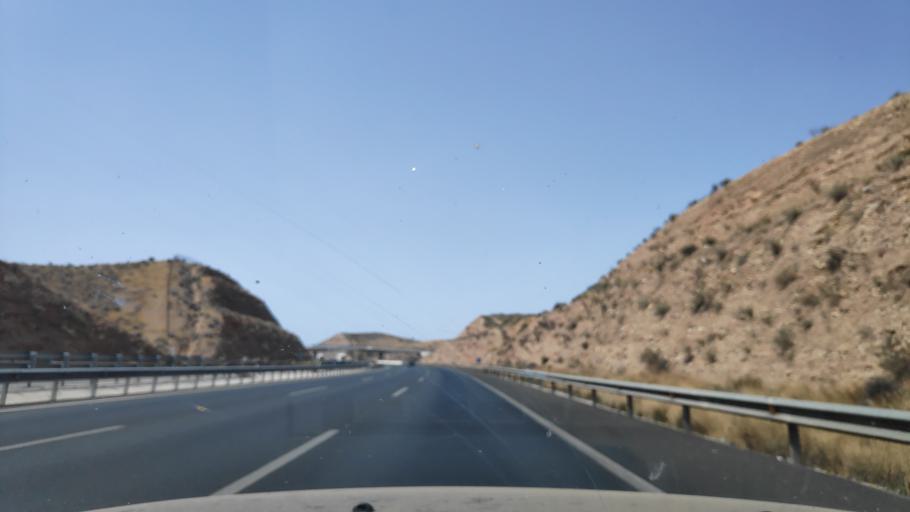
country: ES
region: Murcia
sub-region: Murcia
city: Molina de Segura
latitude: 38.0377
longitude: -1.1606
